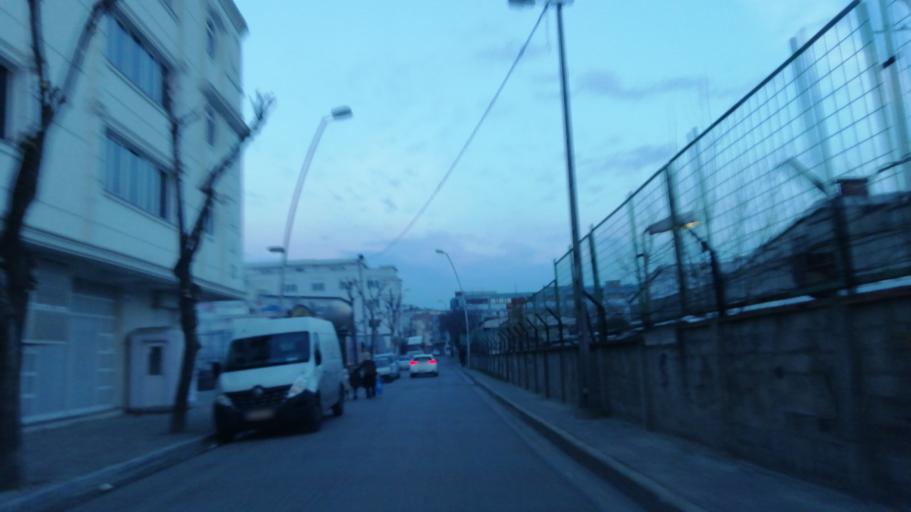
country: TR
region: Istanbul
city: Bahcelievler
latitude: 41.0105
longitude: 28.8237
